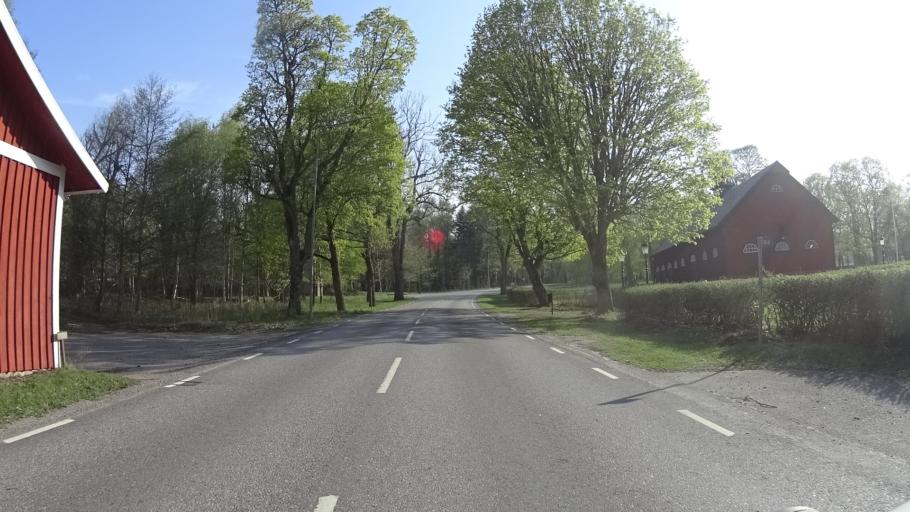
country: SE
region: Vaestra Goetaland
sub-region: Gotene Kommun
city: Goetene
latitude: 58.6251
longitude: 13.4267
